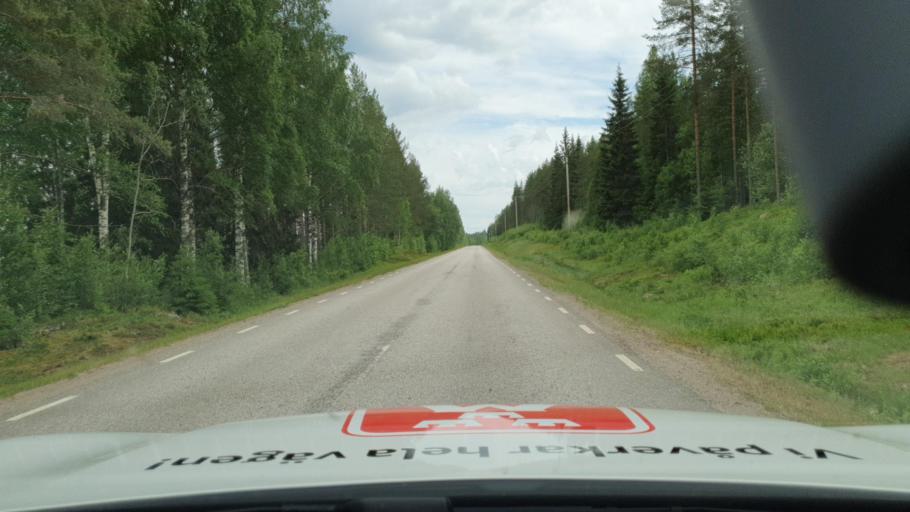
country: NO
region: Hedmark
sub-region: Trysil
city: Innbygda
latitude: 61.0168
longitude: 12.4736
